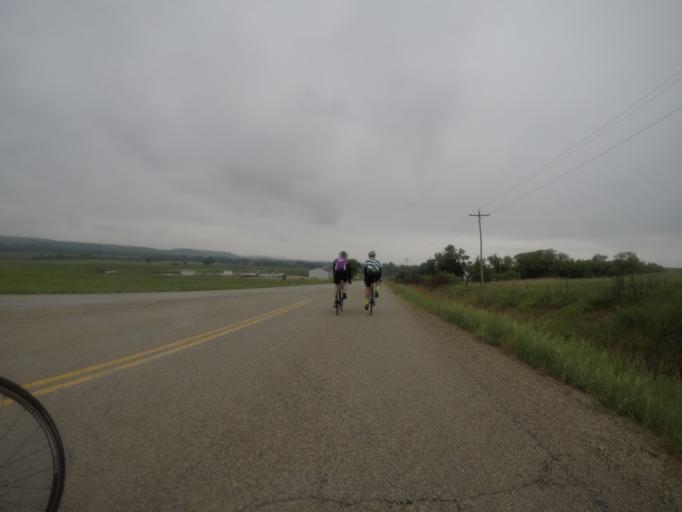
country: US
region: Kansas
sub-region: Pottawatomie County
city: Wamego
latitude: 39.3754
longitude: -96.2214
